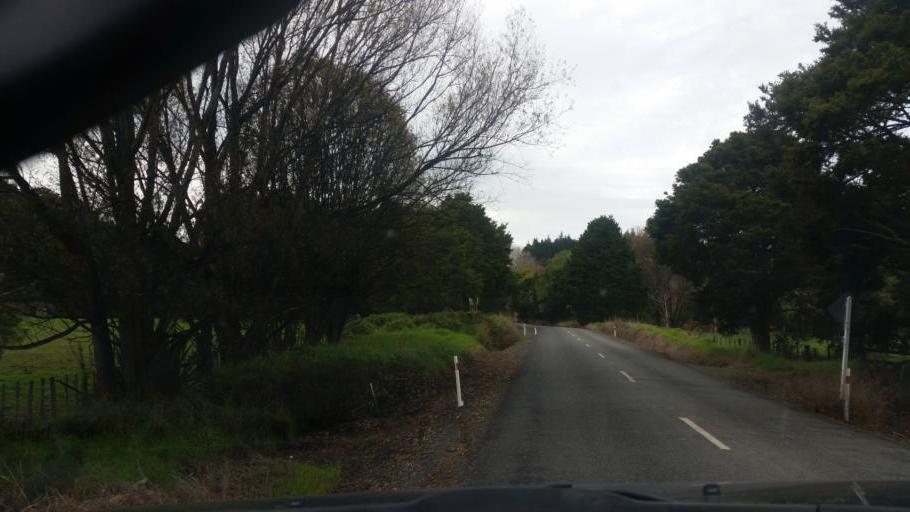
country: NZ
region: Northland
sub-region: Kaipara District
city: Dargaville
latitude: -35.7519
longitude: 173.9027
